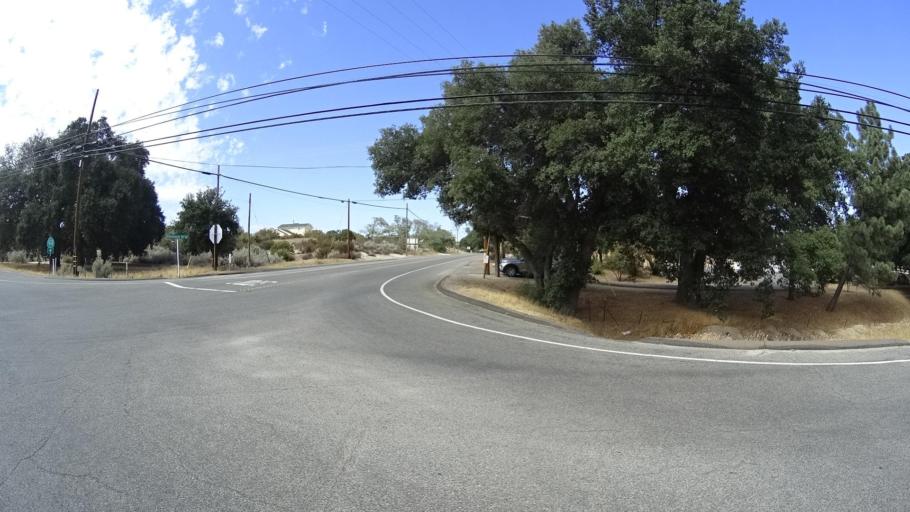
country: MX
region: Baja California
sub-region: Tecate
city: Cereso del Hongo
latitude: 32.6692
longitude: -116.2900
